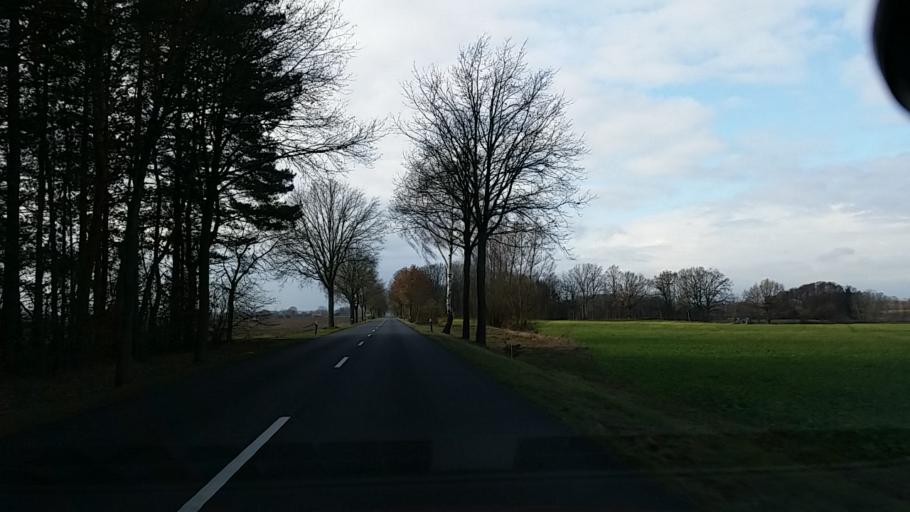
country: DE
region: Lower Saxony
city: Wrestedt
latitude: 52.8826
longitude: 10.6053
